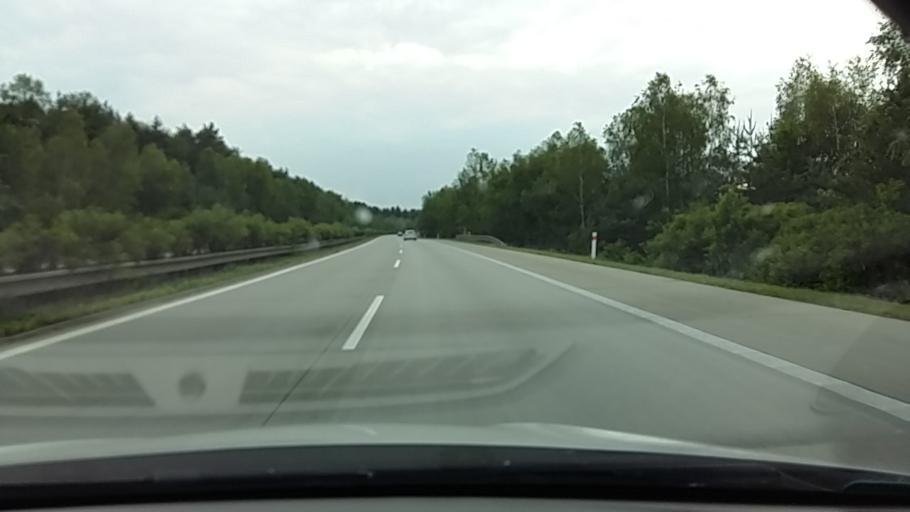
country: CZ
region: Plzensky
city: Line
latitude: 49.7099
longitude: 13.2709
